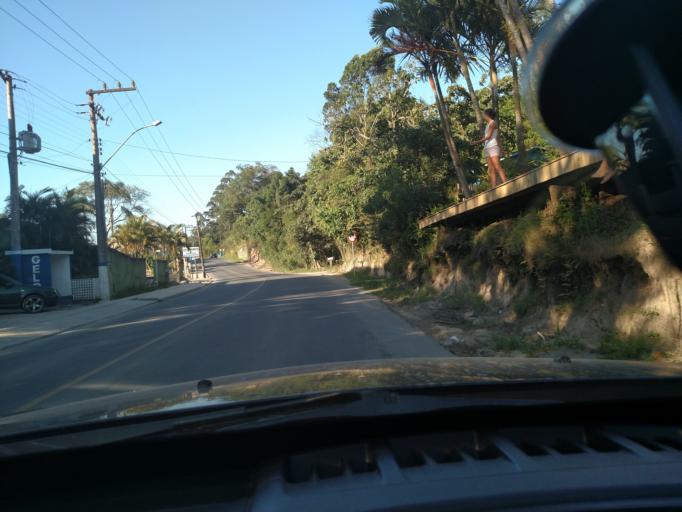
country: BR
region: Santa Catarina
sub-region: Porto Belo
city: Porto Belo
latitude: -27.1693
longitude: -48.5192
